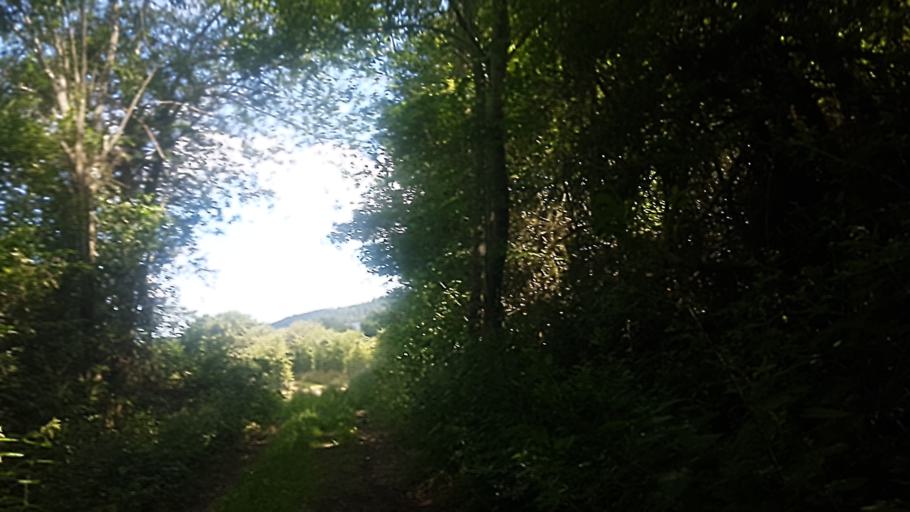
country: BE
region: Wallonia
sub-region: Province de Namur
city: Couvin
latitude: 50.0604
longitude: 4.5531
